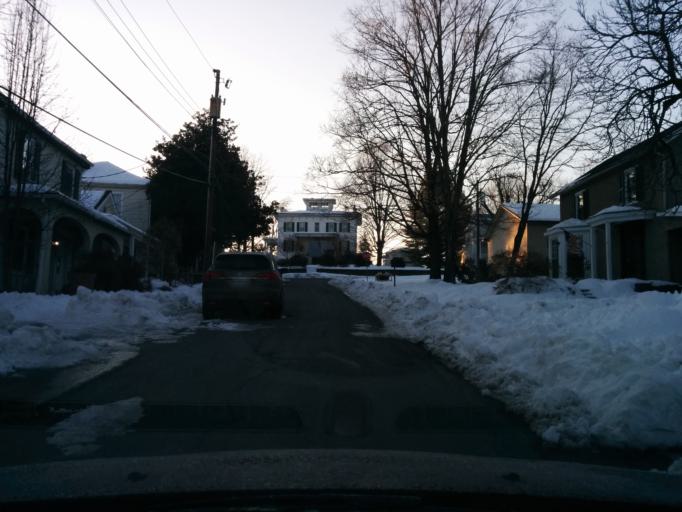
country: US
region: Virginia
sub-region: City of Lexington
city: Lexington
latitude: 37.7851
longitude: -79.4398
